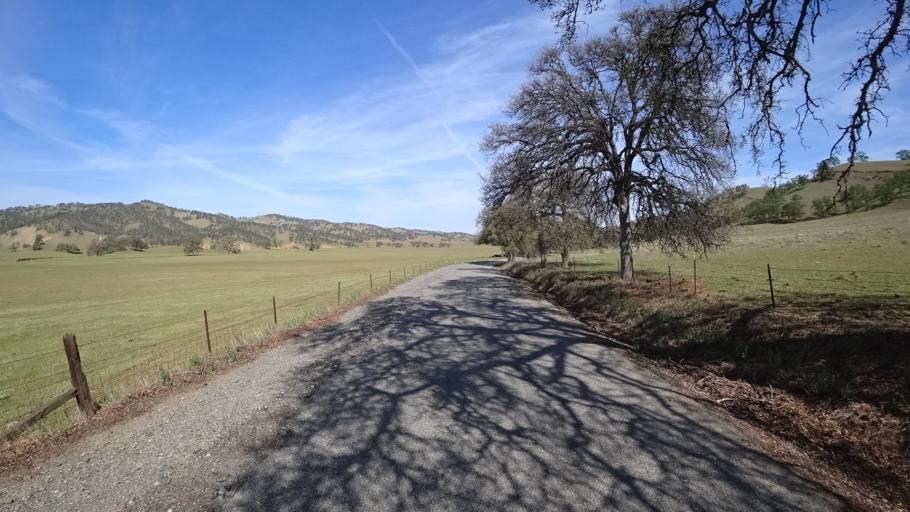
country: US
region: California
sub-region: Glenn County
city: Willows
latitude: 39.5431
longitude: -122.4404
